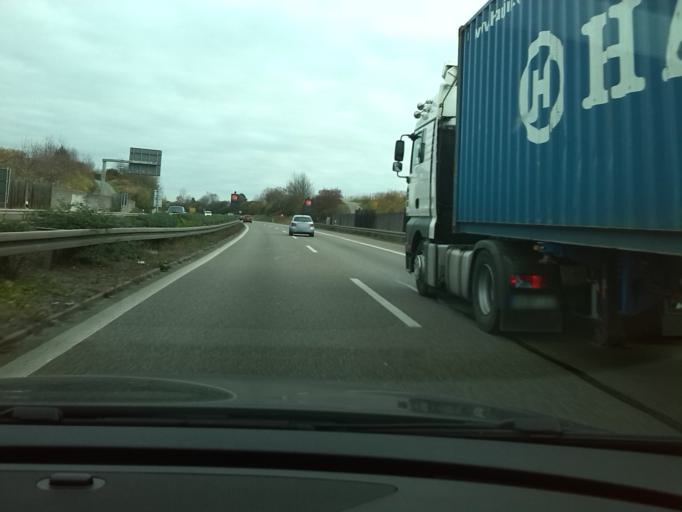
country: DE
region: Baden-Wuerttemberg
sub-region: Regierungsbezirk Stuttgart
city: Fellbach
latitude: 48.7920
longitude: 9.2473
